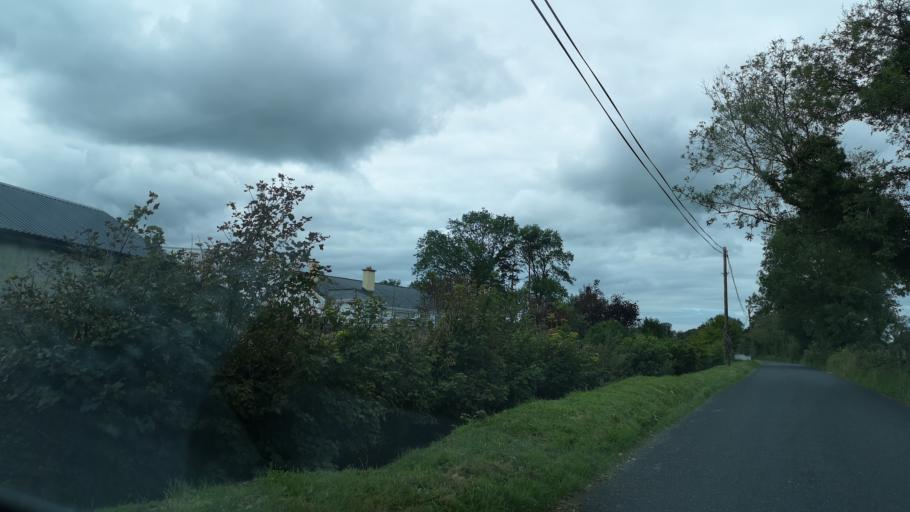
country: IE
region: Connaught
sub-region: County Galway
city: Loughrea
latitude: 53.1613
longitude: -8.4623
